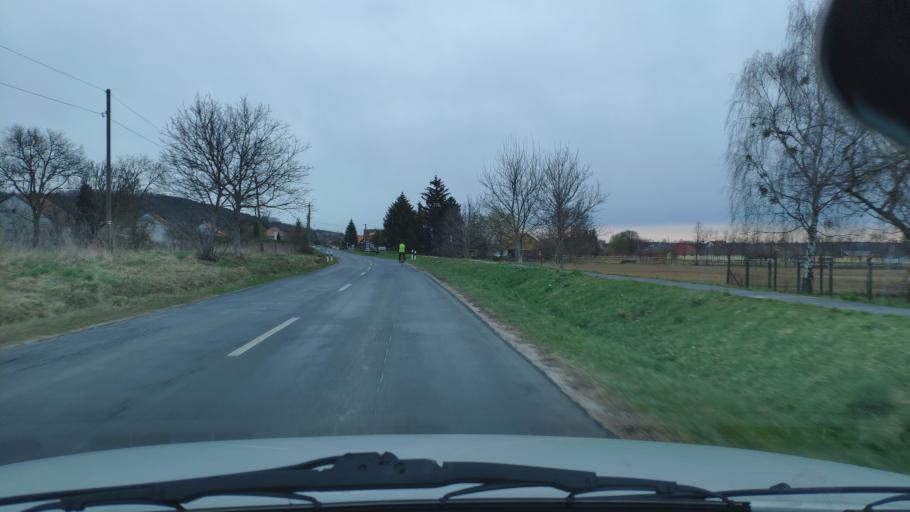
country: HU
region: Zala
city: Nagykanizsa
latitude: 46.5452
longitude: 16.9853
